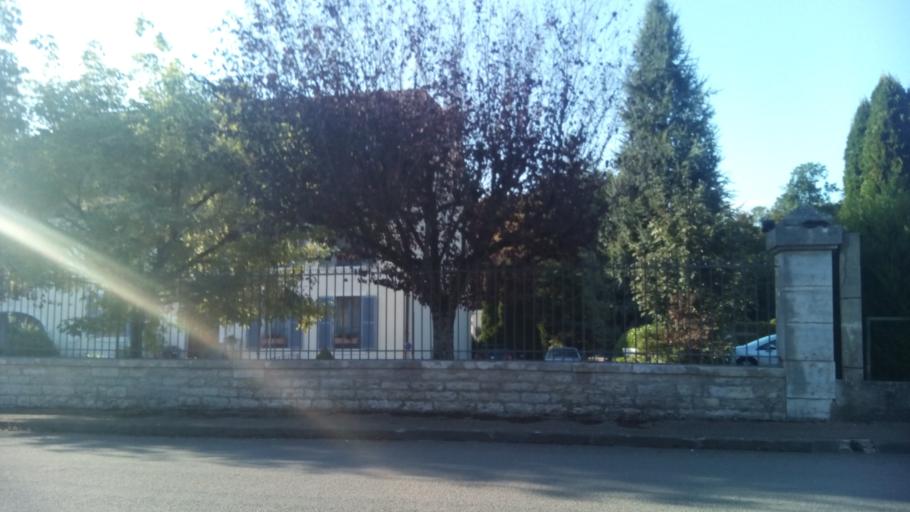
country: FR
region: Franche-Comte
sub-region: Departement de la Haute-Saone
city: Gy
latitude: 47.4071
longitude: 5.8161
